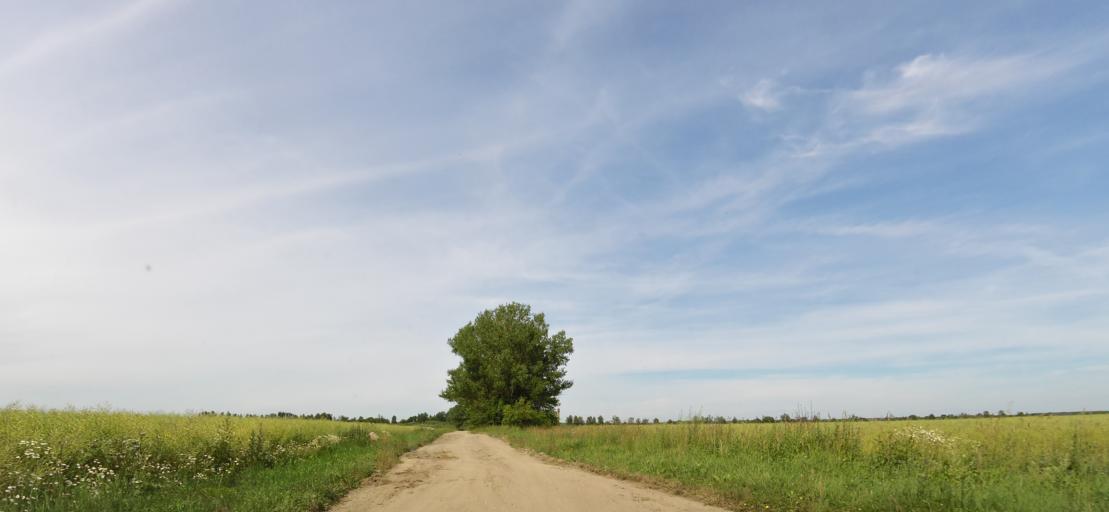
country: LT
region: Panevezys
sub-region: Panevezys City
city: Panevezys
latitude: 55.9100
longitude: 24.2906
